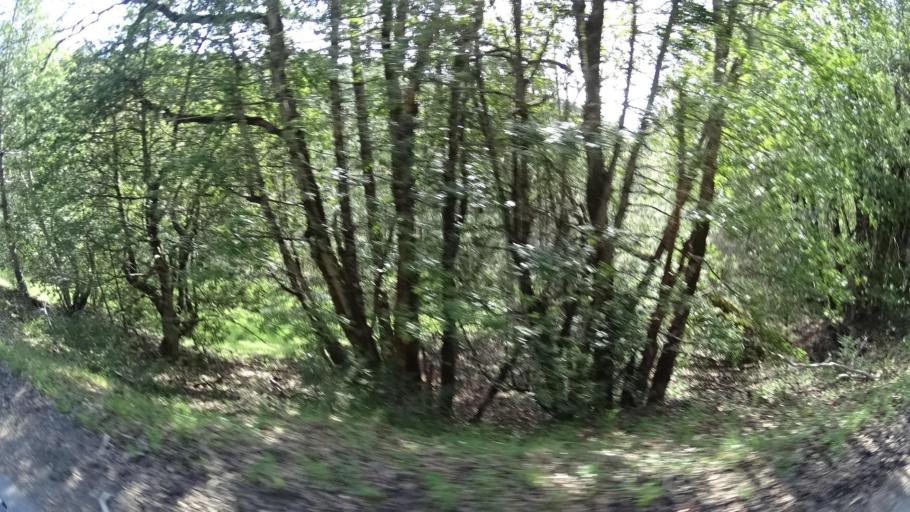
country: US
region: California
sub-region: Humboldt County
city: Hydesville
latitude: 40.6426
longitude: -123.9124
